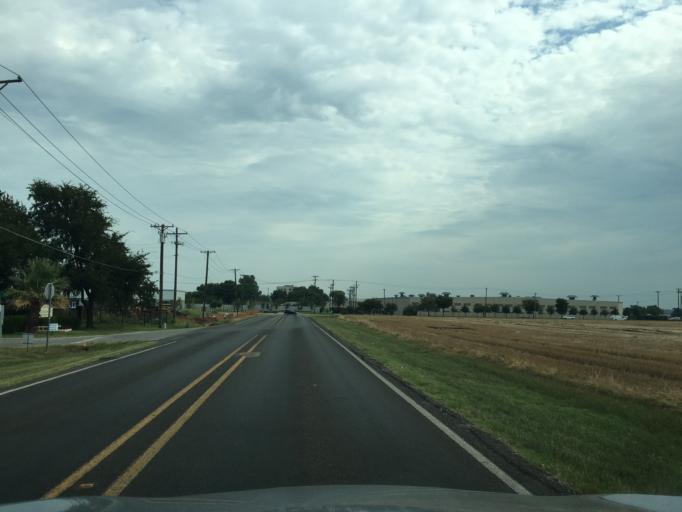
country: US
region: Texas
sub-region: Collin County
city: McKinney
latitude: 33.1761
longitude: -96.6005
